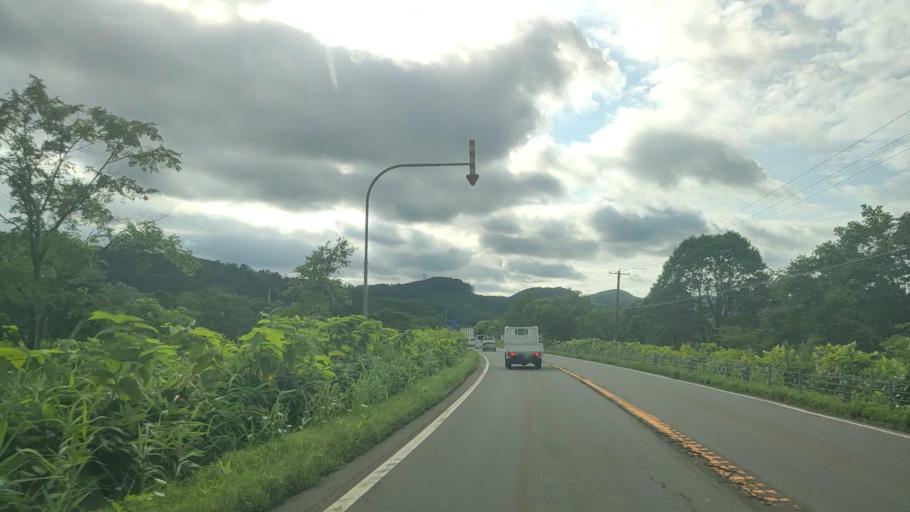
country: JP
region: Hokkaido
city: Niseko Town
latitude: 42.6012
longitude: 140.4930
